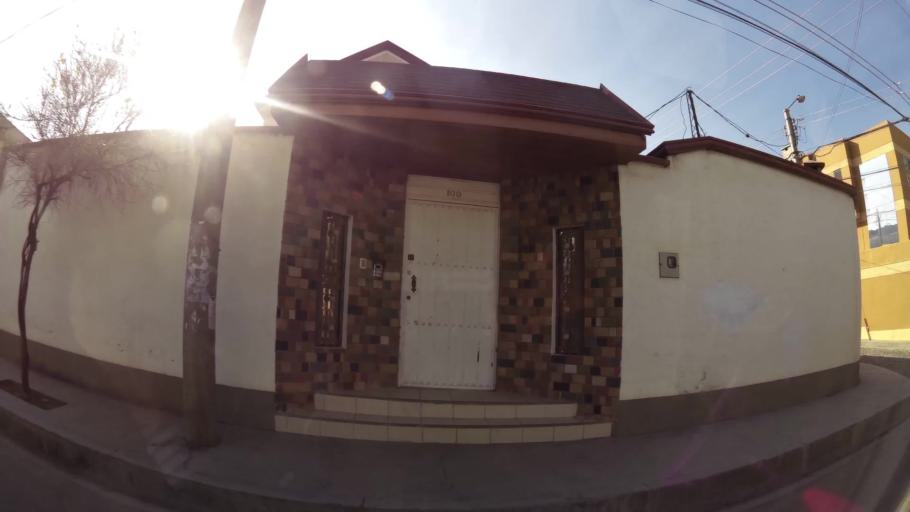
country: BO
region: La Paz
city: La Paz
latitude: -16.5011
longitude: -68.0828
